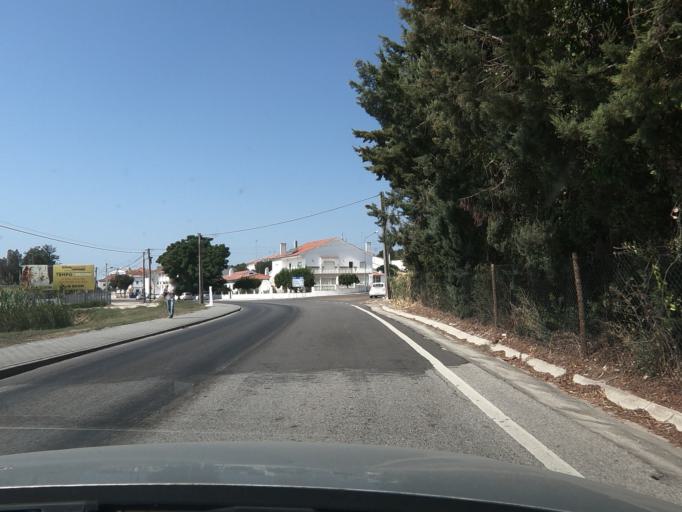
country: PT
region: Setubal
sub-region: Alcacer do Sal
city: Alcacer do Sal
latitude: 38.3696
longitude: -8.4987
